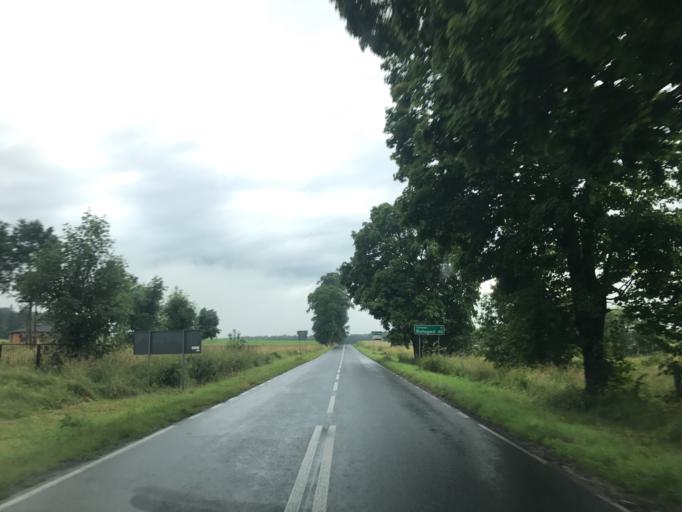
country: PL
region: West Pomeranian Voivodeship
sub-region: Powiat koszalinski
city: Bobolice
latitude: 53.9911
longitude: 16.4770
